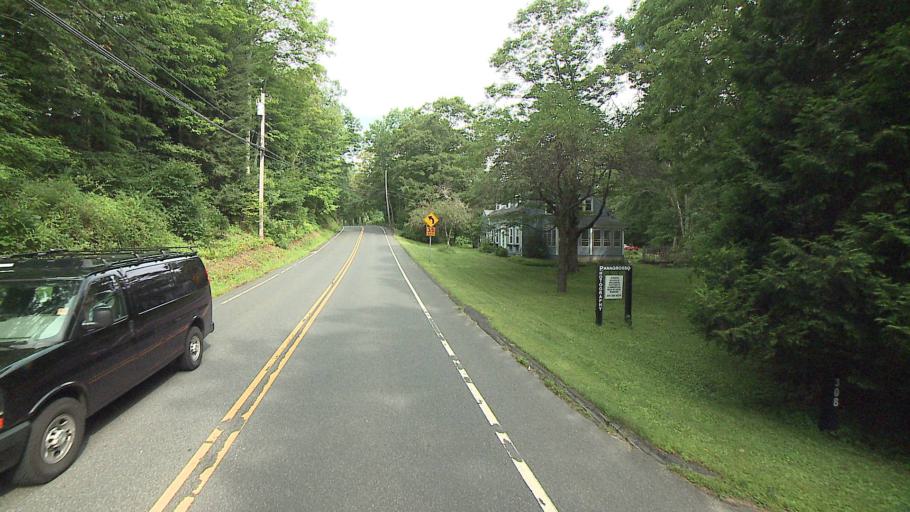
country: US
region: Connecticut
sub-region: Litchfield County
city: Woodbury
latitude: 41.5680
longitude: -73.2201
